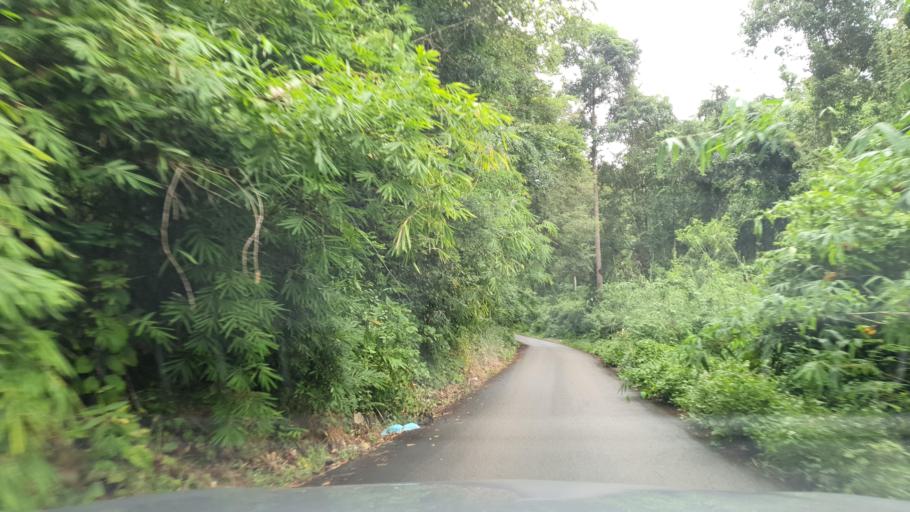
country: TH
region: Chiang Mai
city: Mae Taeng
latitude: 19.2115
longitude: 98.9289
